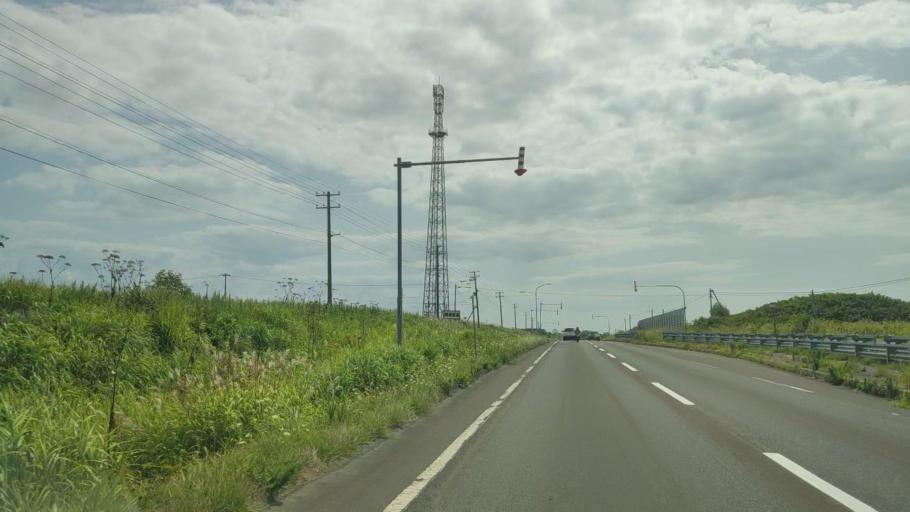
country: JP
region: Hokkaido
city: Rumoi
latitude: 44.4369
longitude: 141.7514
